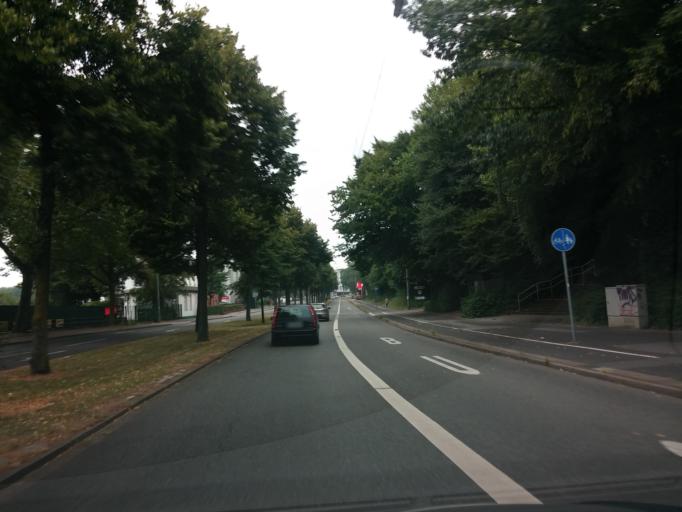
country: DE
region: North Rhine-Westphalia
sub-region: Regierungsbezirk Munster
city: Gladbeck
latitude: 51.5879
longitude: 7.0500
